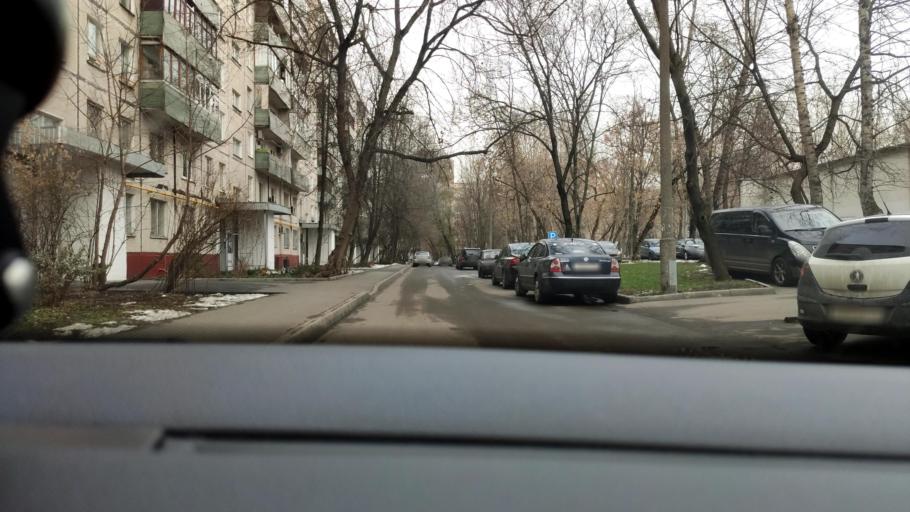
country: RU
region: Moscow
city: Tekstil'shchiki
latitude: 55.7024
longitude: 37.7383
